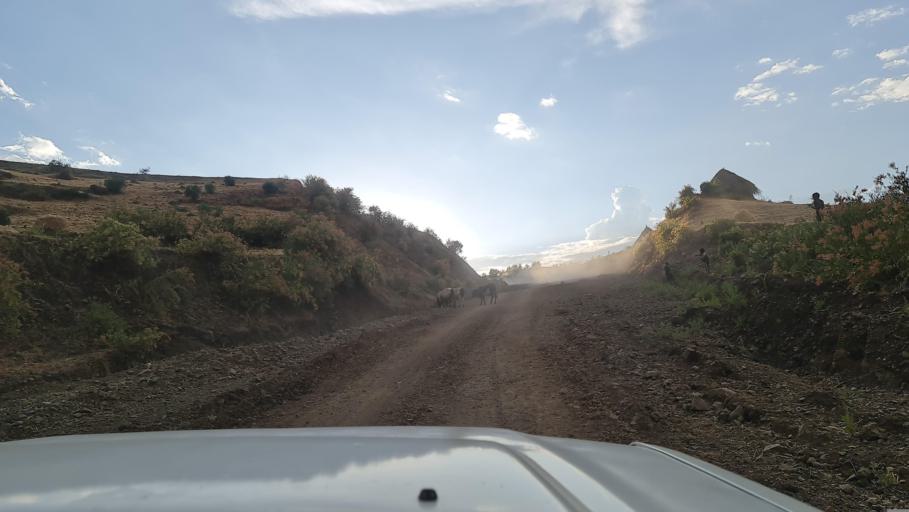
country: ET
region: Amhara
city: Debark'
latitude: 13.0286
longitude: 38.0542
